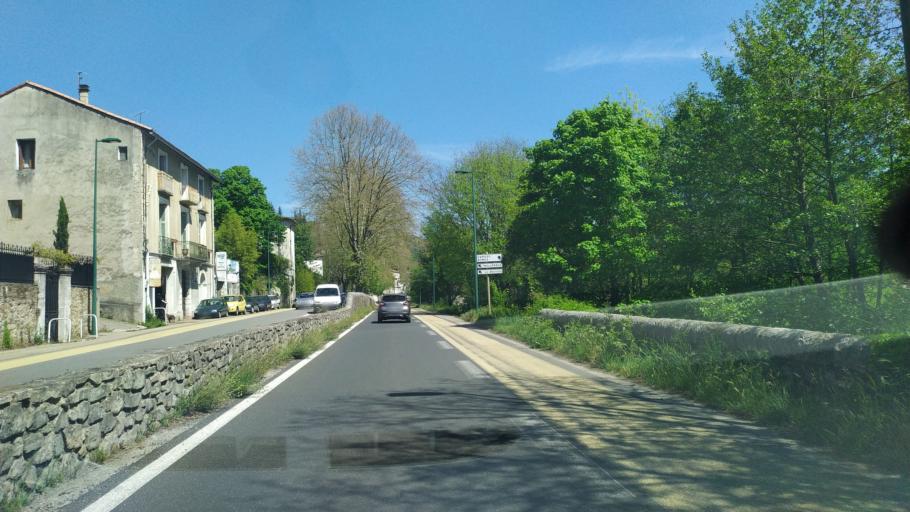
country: FR
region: Languedoc-Roussillon
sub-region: Departement du Gard
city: Le Vigan
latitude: 43.9922
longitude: 3.6138
